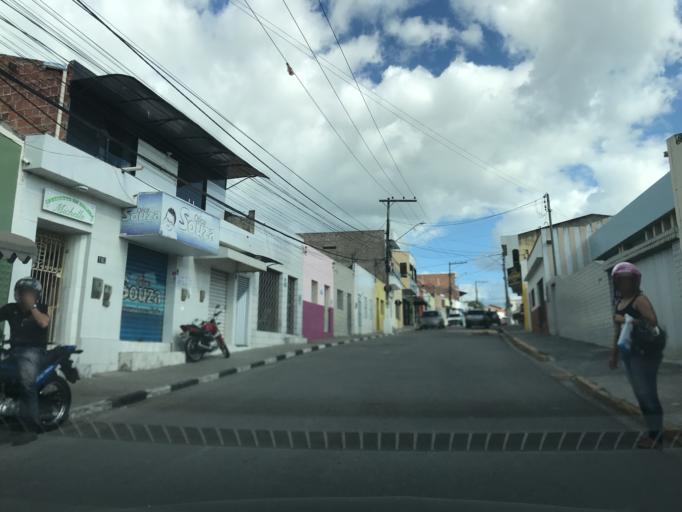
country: BR
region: Pernambuco
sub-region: Bezerros
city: Bezerros
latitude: -8.2362
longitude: -35.7527
